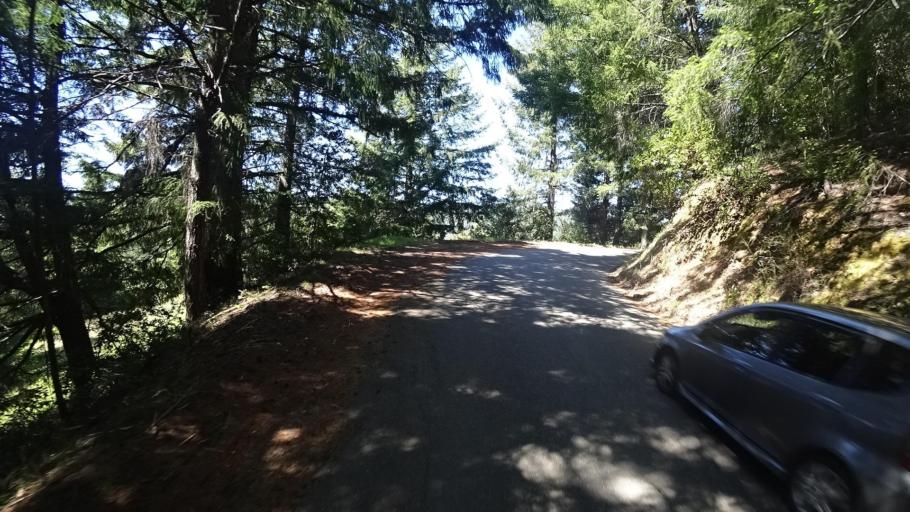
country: US
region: California
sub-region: Humboldt County
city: Redway
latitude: 40.1502
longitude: -124.0346
